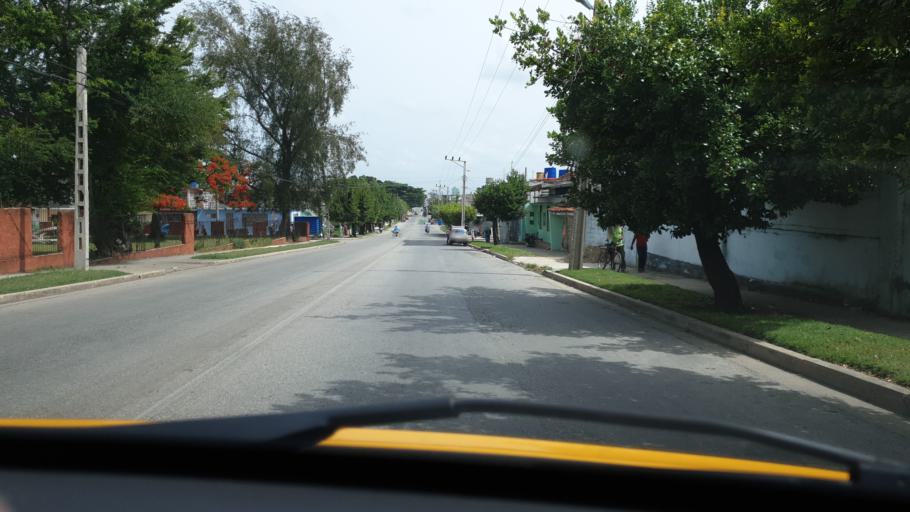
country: CU
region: Villa Clara
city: Santa Clara
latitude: 22.3911
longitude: -79.9605
